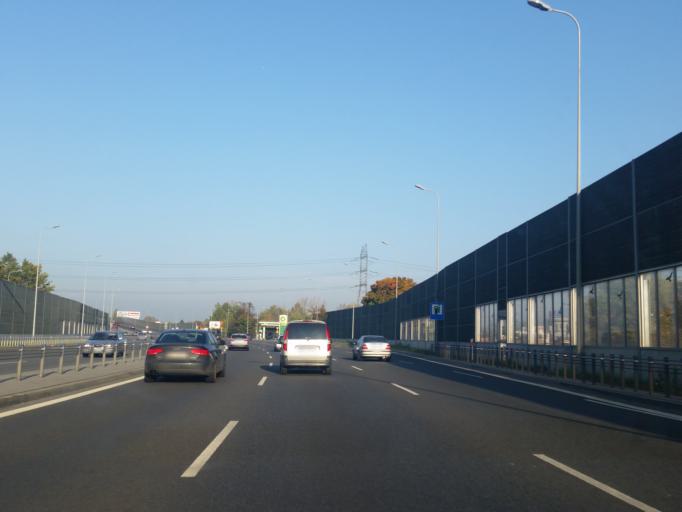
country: PL
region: Masovian Voivodeship
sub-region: Powiat warszawski zachodni
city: Lomianki
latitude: 52.3258
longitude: 20.9084
